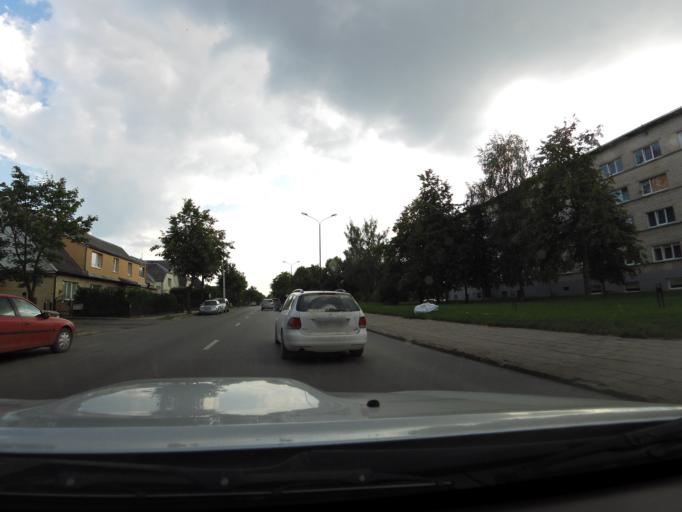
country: LT
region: Siauliu apskritis
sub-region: Siauliai
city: Siauliai
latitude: 55.9474
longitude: 23.3122
